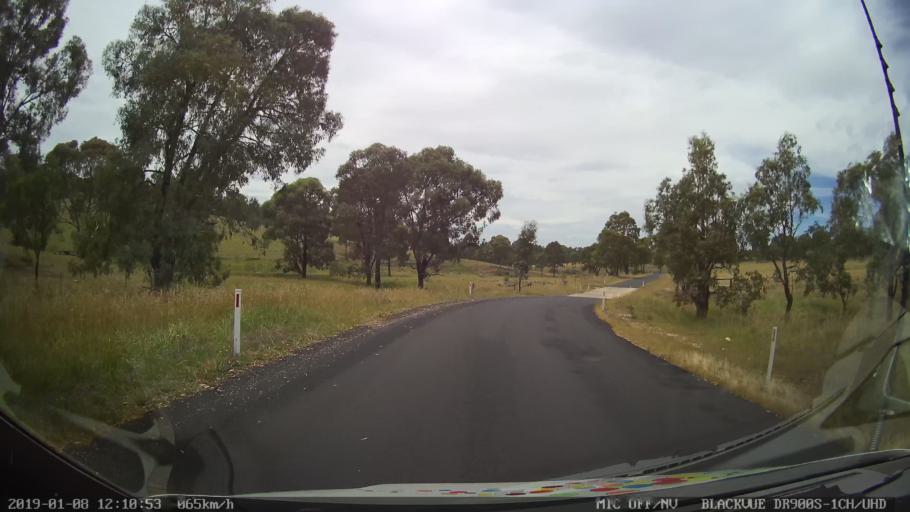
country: AU
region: New South Wales
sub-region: Armidale Dumaresq
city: Armidale
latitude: -30.4471
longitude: 151.5911
